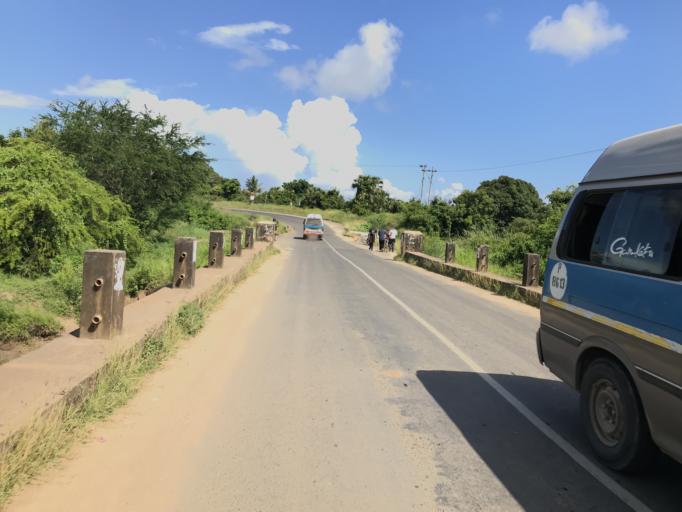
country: TZ
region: Dar es Salaam
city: Dar es Salaam
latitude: -6.8898
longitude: 39.4267
